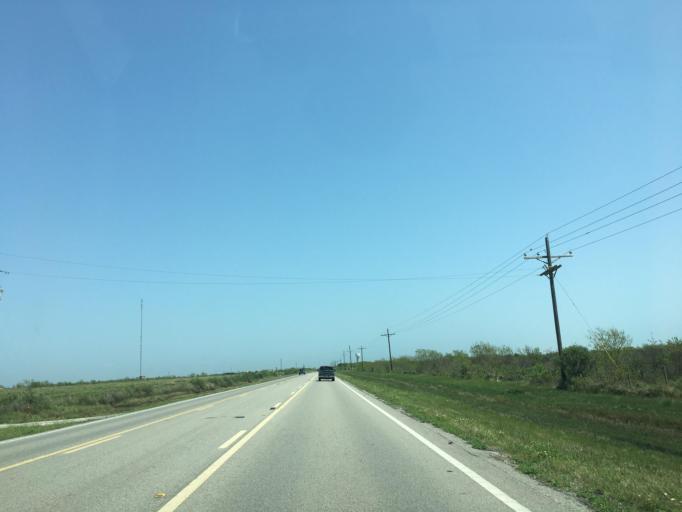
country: US
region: Texas
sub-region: Galveston County
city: Galveston
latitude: 29.4091
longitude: -94.7166
